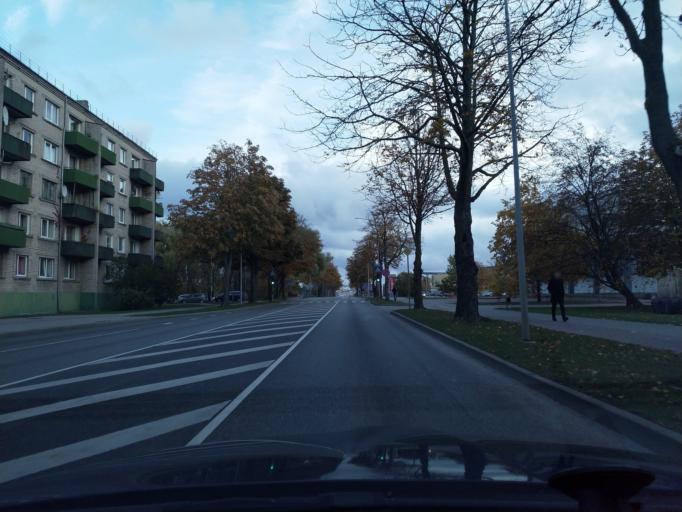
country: LV
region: Ventspils
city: Ventspils
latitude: 57.3891
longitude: 21.5768
